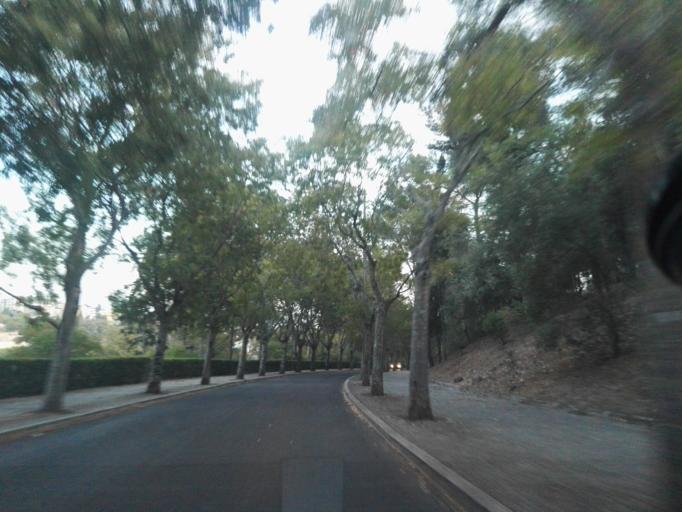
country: PT
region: Lisbon
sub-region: Oeiras
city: Quejas
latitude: 38.7079
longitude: -9.2582
